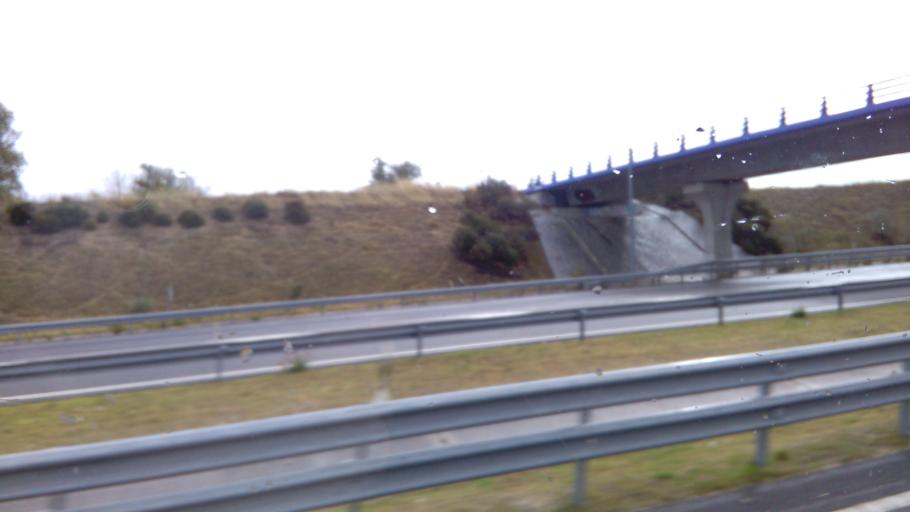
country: ES
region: Madrid
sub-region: Provincia de Madrid
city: Alcorcon
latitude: 40.3274
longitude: -3.8162
